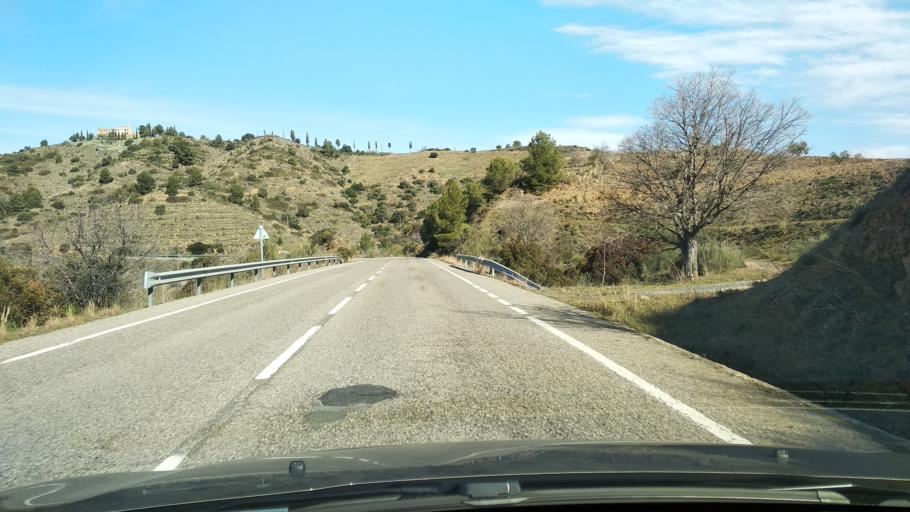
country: ES
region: Catalonia
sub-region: Provincia de Tarragona
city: Falset
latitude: 41.2022
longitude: 0.7812
